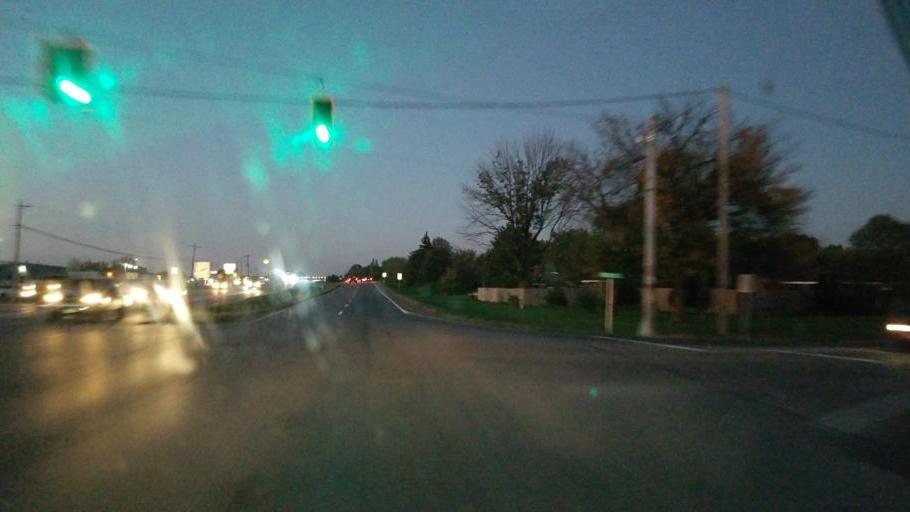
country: US
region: Ohio
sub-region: Pickaway County
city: Logan Elm Village
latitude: 39.5669
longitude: -82.9547
